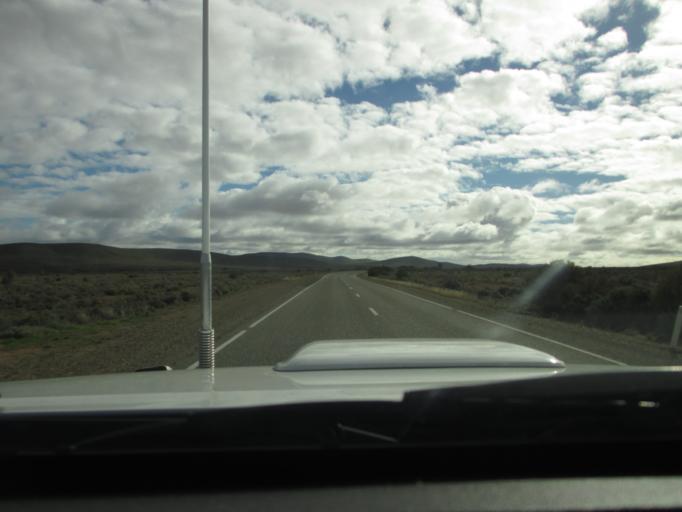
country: AU
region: South Australia
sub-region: Flinders Ranges
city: Quorn
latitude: -32.2421
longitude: 138.5127
